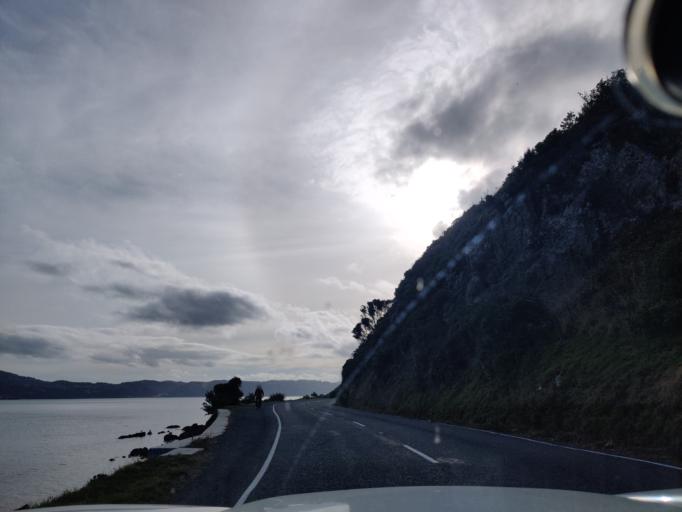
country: NZ
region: Wellington
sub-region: Wellington City
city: Wellington
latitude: -41.3071
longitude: 174.8143
